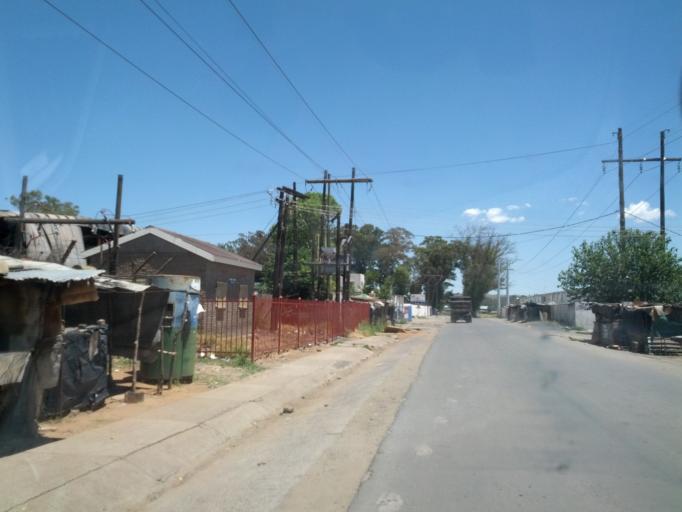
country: LS
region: Maseru
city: Maseru
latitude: -29.2967
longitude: 27.4690
